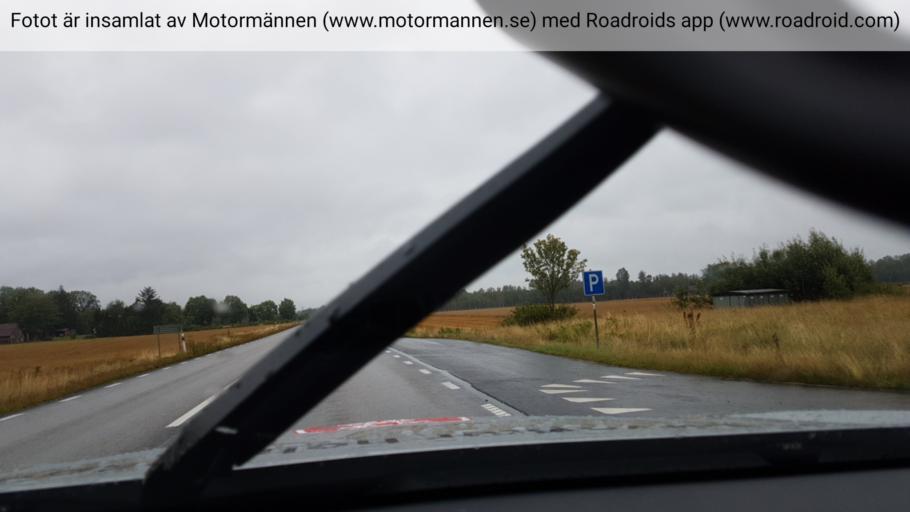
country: SE
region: Vaestra Goetaland
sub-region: Melleruds Kommun
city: Mellerud
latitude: 58.6492
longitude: 12.4152
